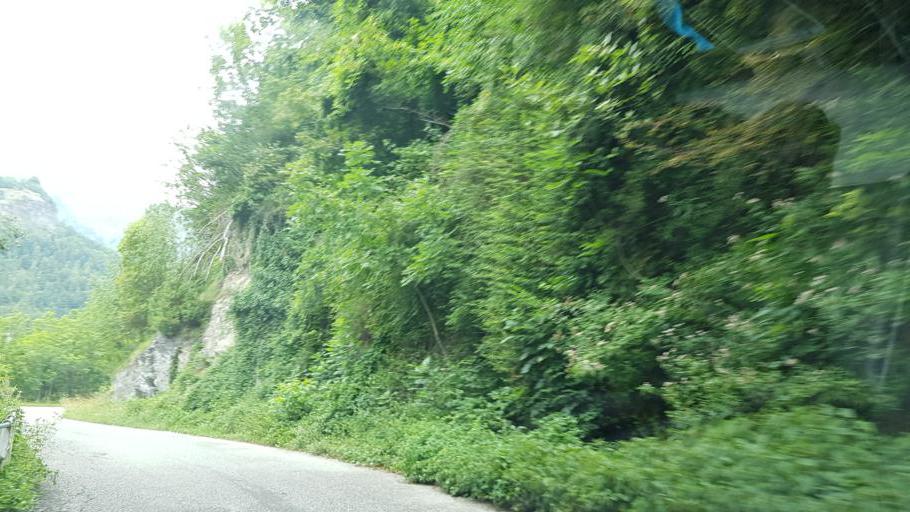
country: IT
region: Piedmont
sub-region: Provincia di Cuneo
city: Stroppo
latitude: 44.5057
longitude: 7.1250
